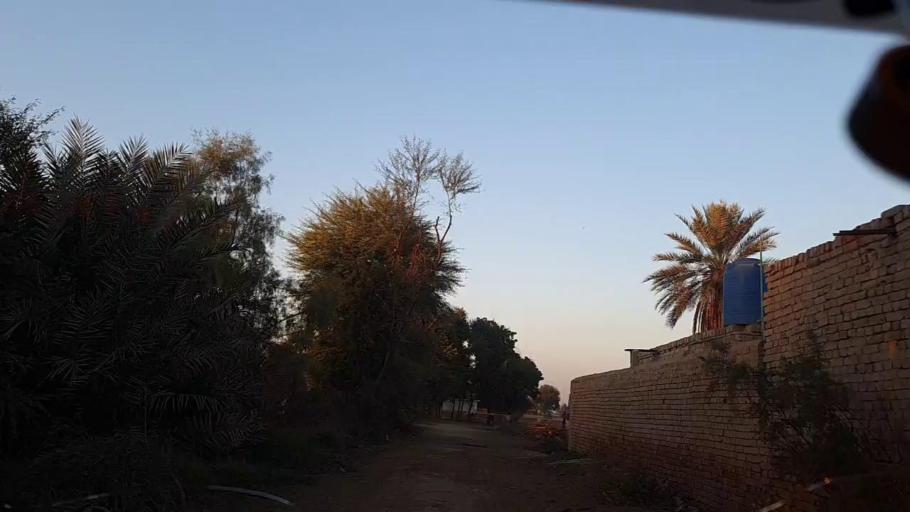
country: PK
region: Sindh
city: Adilpur
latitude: 27.8429
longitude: 69.2961
